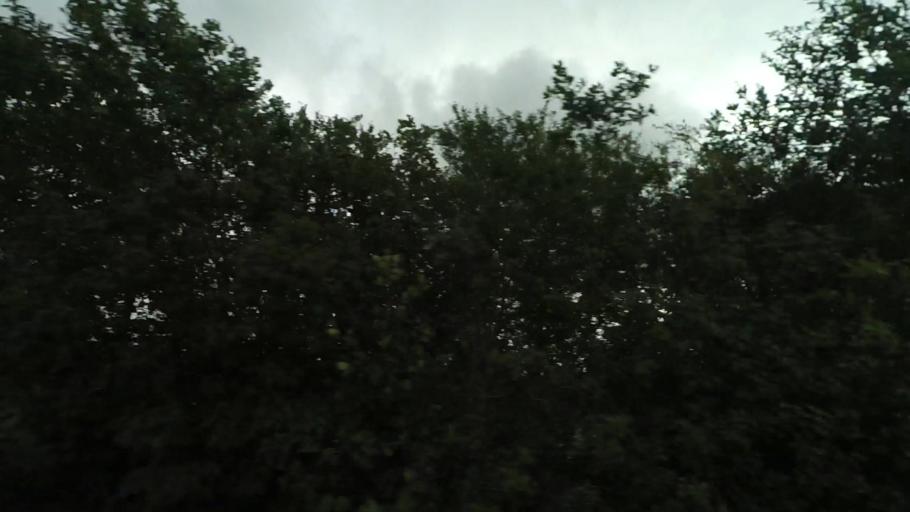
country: DK
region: Central Jutland
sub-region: Syddjurs Kommune
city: Ryomgard
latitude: 56.3902
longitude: 10.5656
